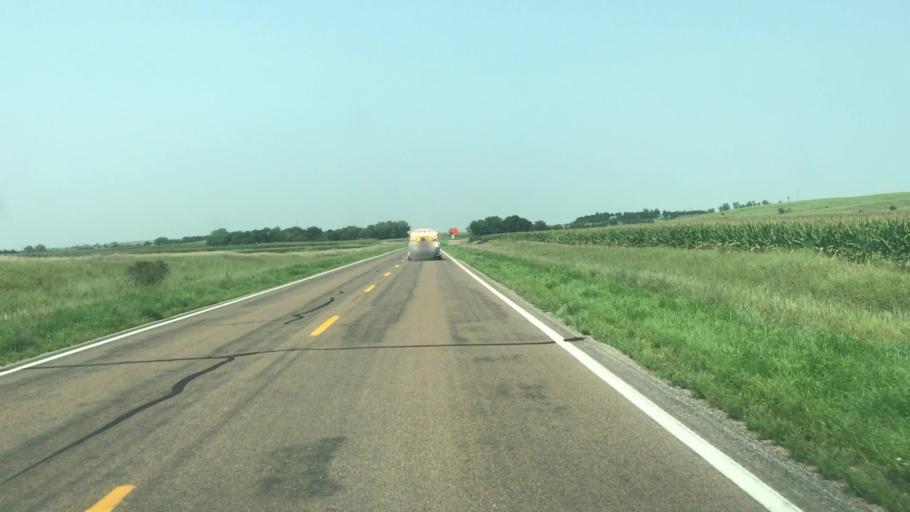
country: US
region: Nebraska
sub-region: Sherman County
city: Loup City
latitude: 41.2539
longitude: -98.9390
